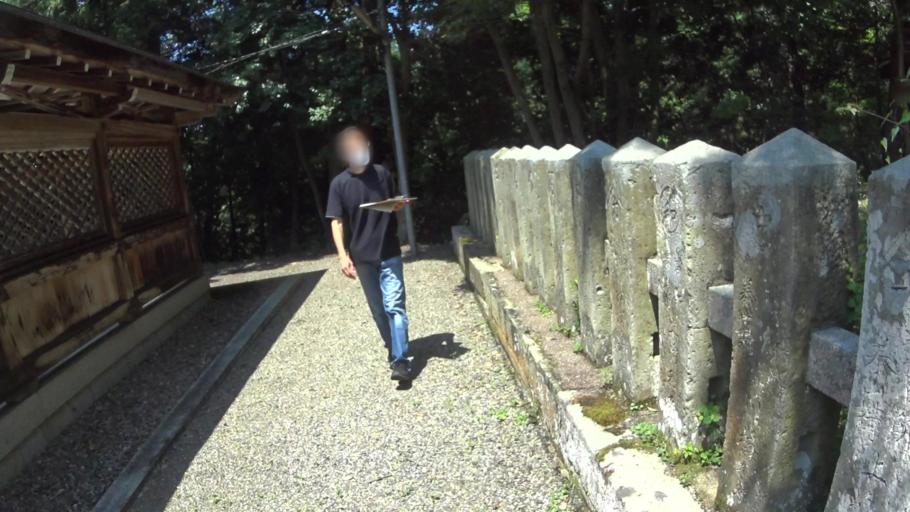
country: JP
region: Kyoto
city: Miyazu
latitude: 35.6206
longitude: 135.0620
